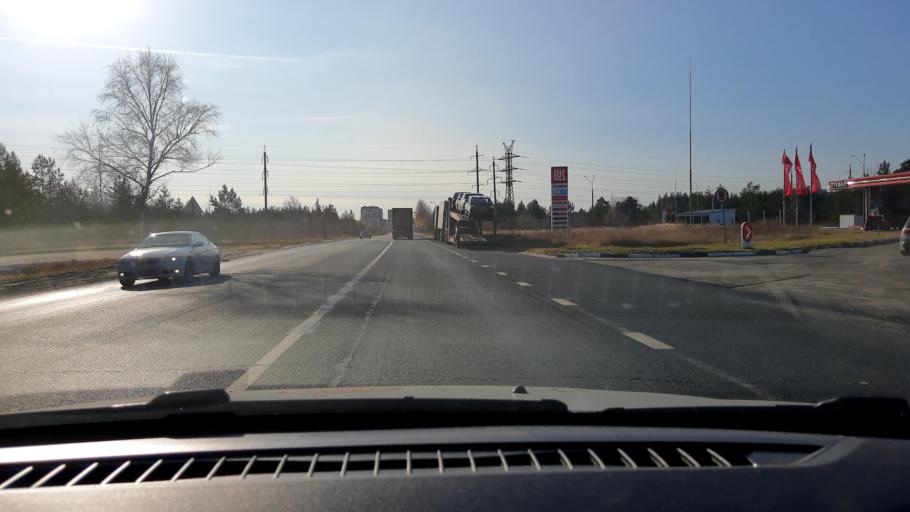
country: RU
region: Nizjnij Novgorod
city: Dzerzhinsk
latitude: 56.2627
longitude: 43.4689
